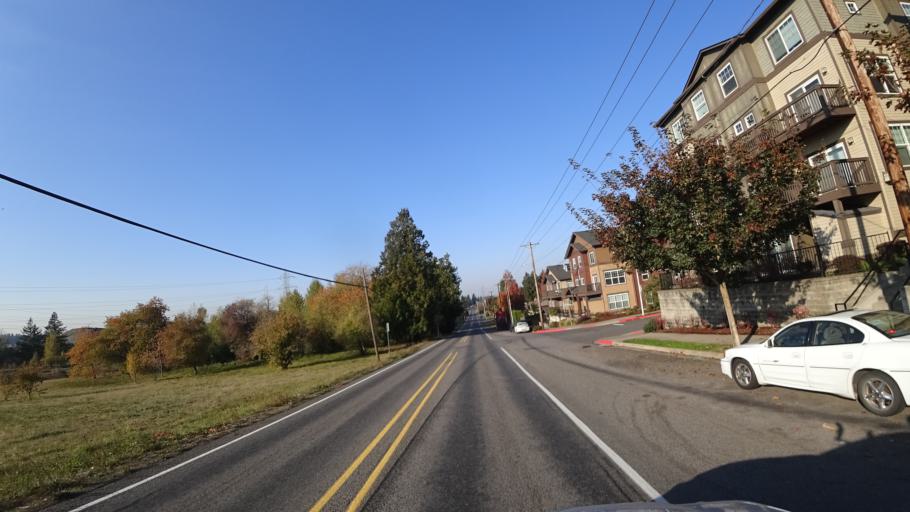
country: US
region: Oregon
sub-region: Multnomah County
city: Gresham
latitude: 45.5058
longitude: -122.4550
